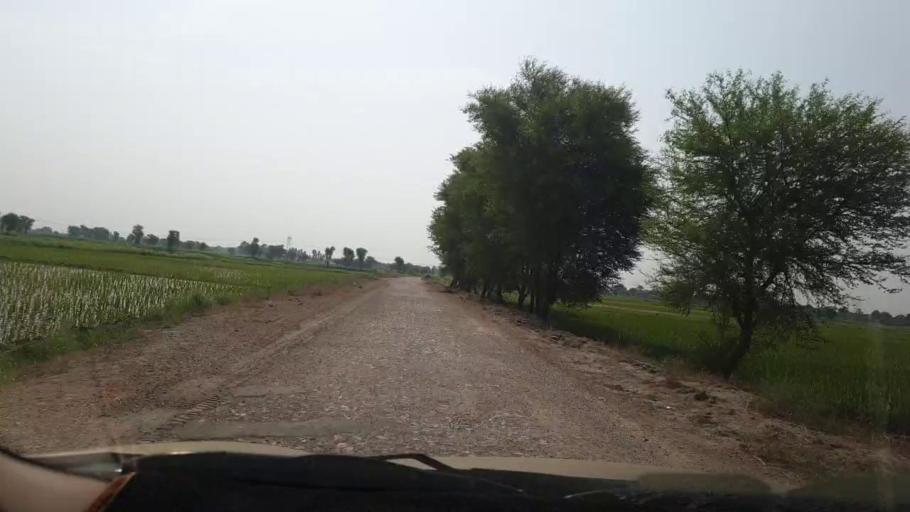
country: PK
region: Sindh
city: Goth Garelo
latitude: 27.4381
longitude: 68.0405
